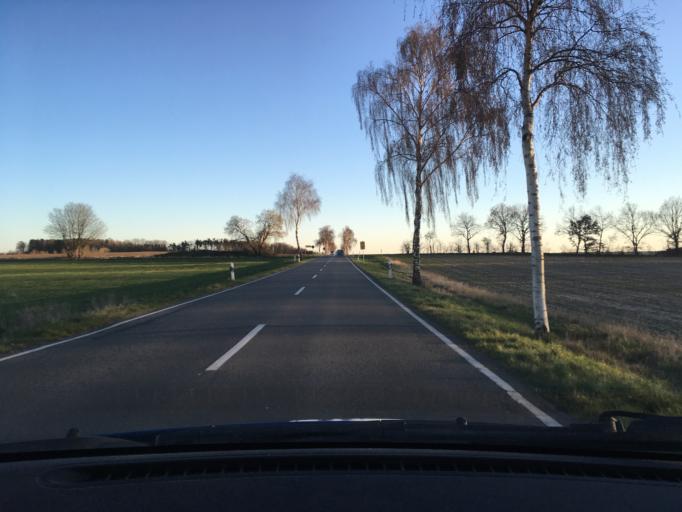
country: DE
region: Lower Saxony
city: Dahlem
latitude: 53.2044
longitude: 10.7519
